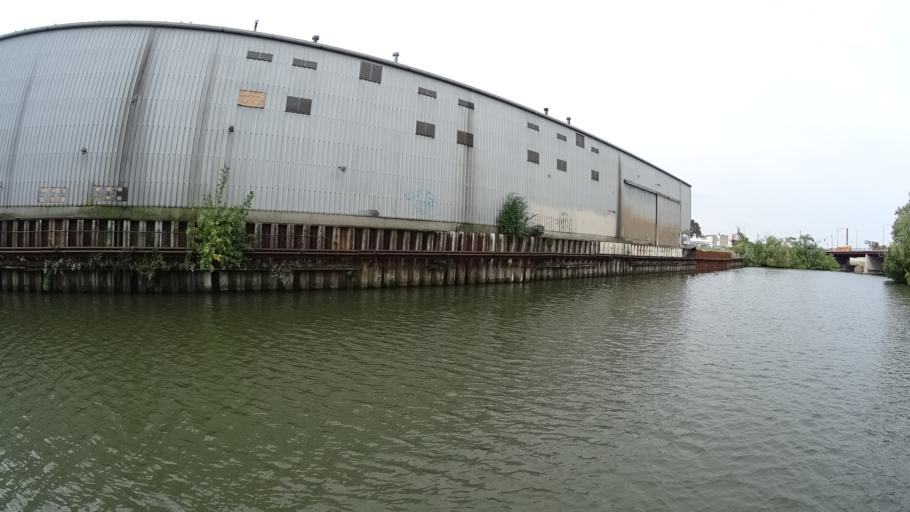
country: US
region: Illinois
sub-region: Cook County
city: Chicago
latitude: 41.9236
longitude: -87.6733
